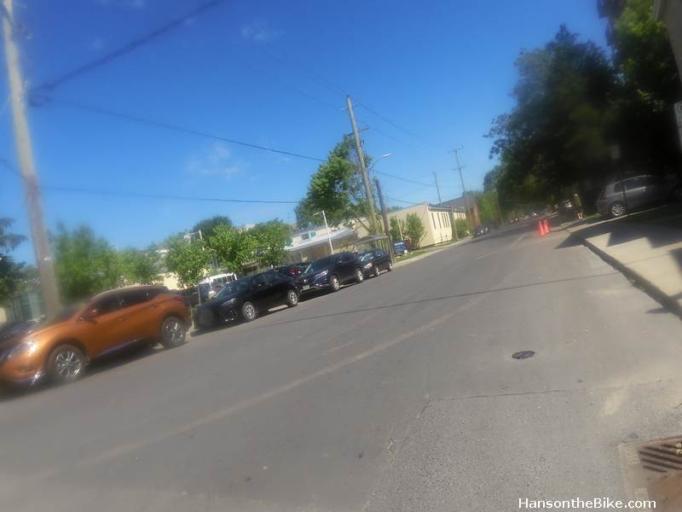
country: CA
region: Ontario
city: Kingston
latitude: 44.2337
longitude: -76.4837
